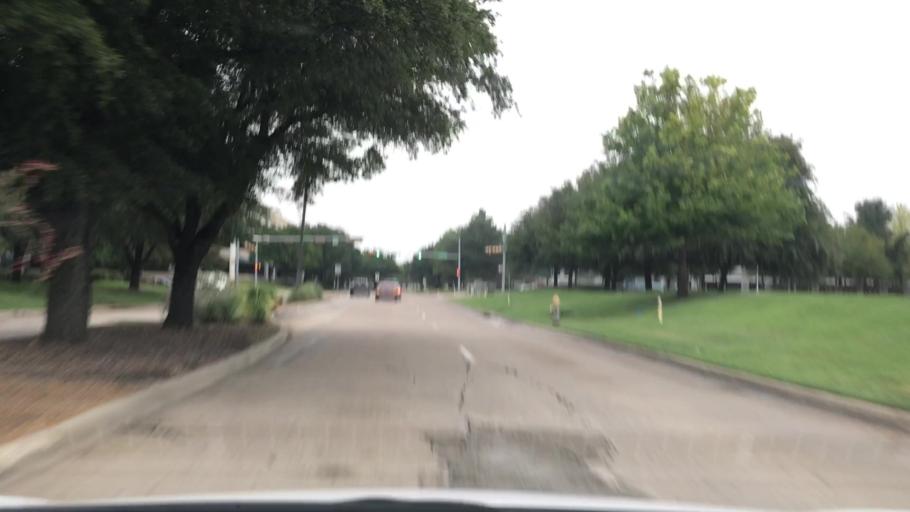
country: US
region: Texas
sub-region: Dallas County
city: Coppell
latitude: 32.9274
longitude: -97.0100
